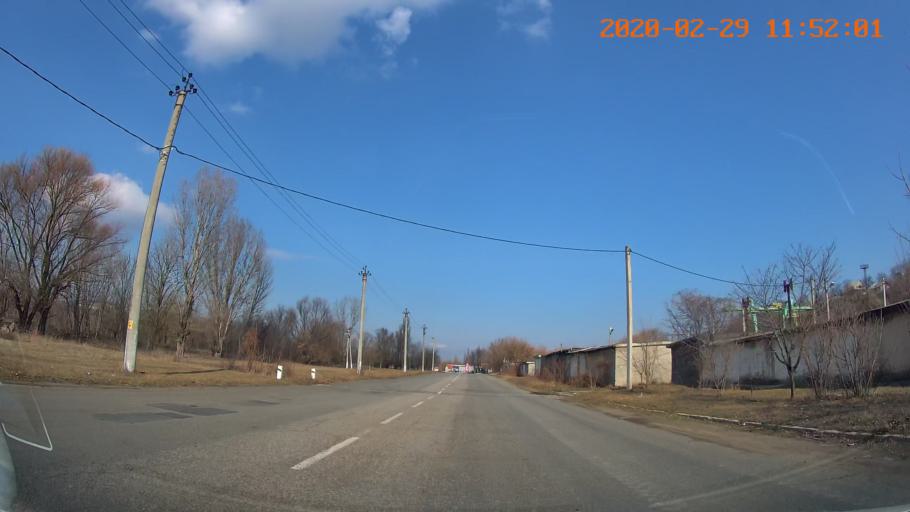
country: MD
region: Telenesti
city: Ribnita
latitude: 47.7689
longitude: 28.9912
